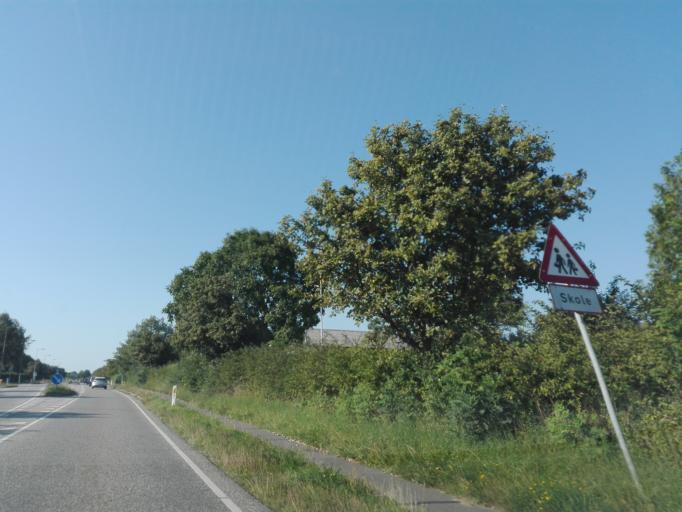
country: DK
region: Central Jutland
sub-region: Odder Kommune
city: Odder
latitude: 55.9184
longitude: 10.2500
